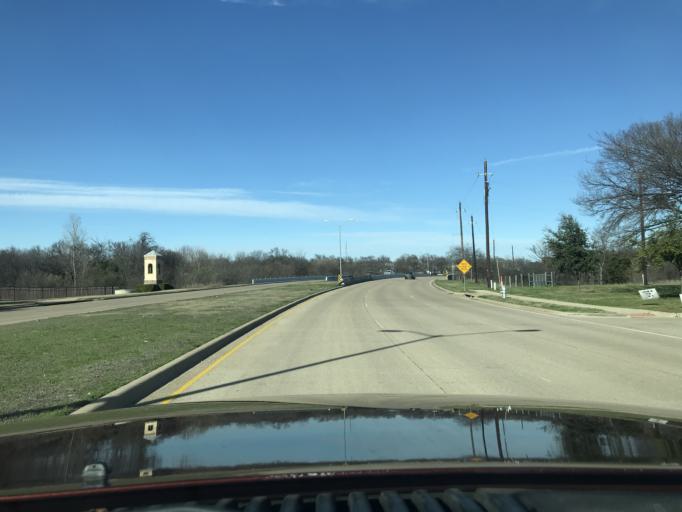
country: US
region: Texas
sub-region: Tarrant County
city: Edgecliff Village
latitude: 32.6586
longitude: -97.3338
